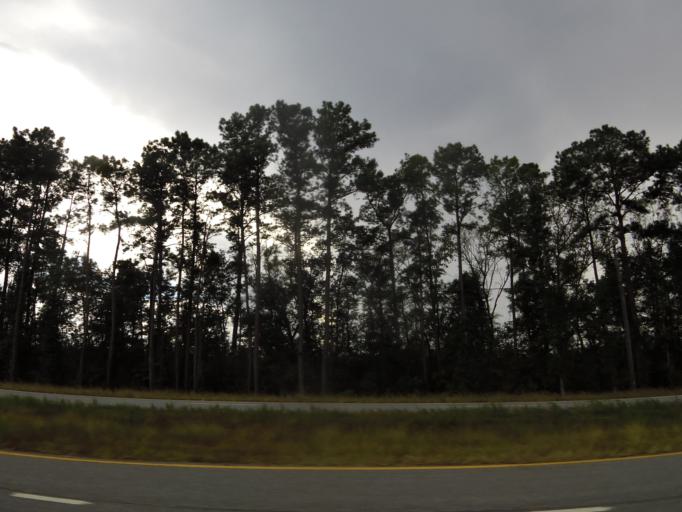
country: US
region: Georgia
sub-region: McIntosh County
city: Darien
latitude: 31.3747
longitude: -81.6285
